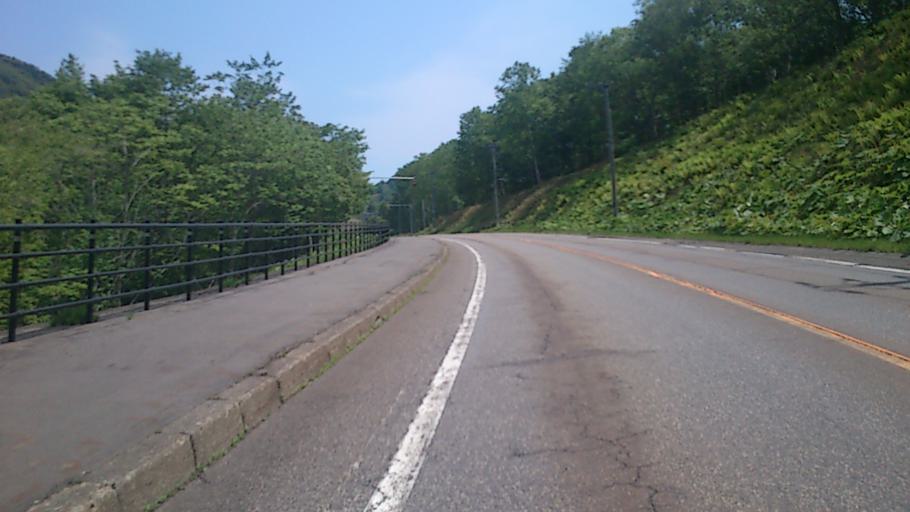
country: JP
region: Hokkaido
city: Otofuke
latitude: 43.3609
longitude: 143.2480
